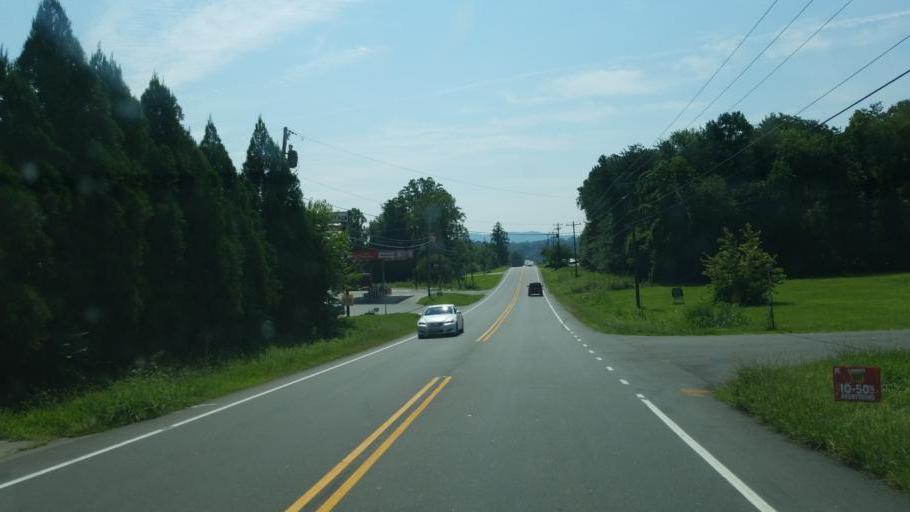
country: US
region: North Carolina
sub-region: Burke County
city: Morganton
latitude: 35.7565
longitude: -81.7242
